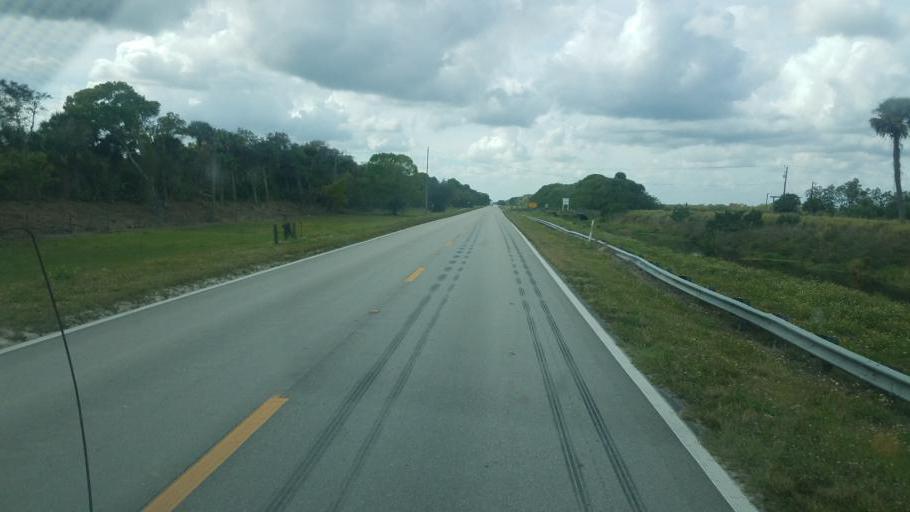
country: US
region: Florida
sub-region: Indian River County
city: West Vero Corridor
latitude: 27.4484
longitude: -80.6271
